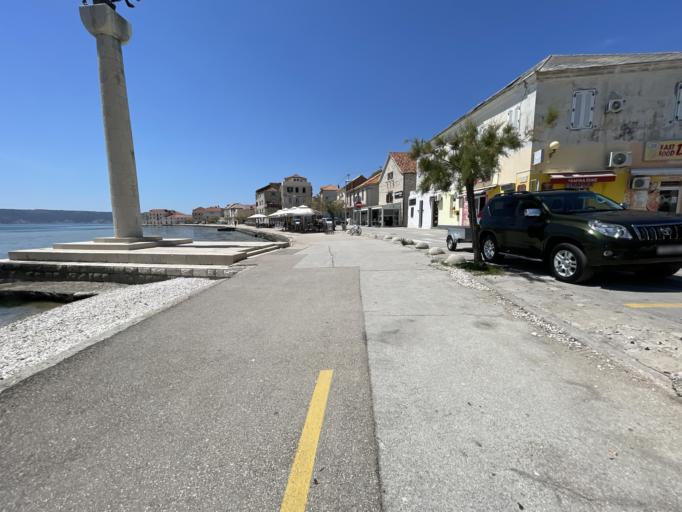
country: HR
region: Splitsko-Dalmatinska
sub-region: Grad Trogir
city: Trogir
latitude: 43.5495
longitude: 16.3417
